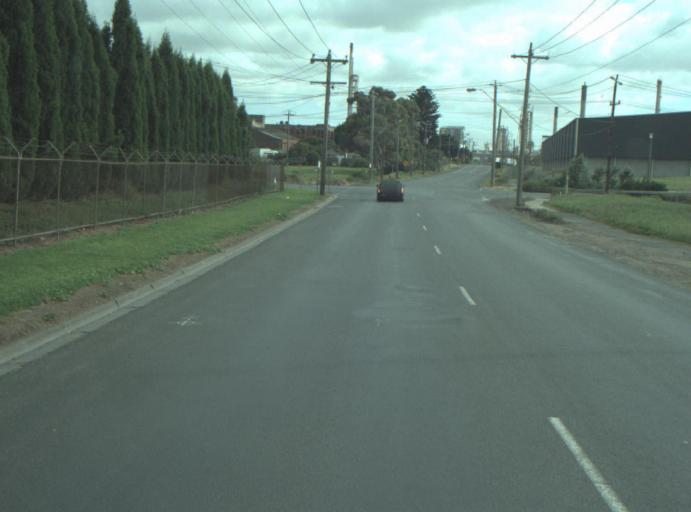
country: AU
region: Victoria
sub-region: Greater Geelong
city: Bell Park
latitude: -38.0870
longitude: 144.3740
